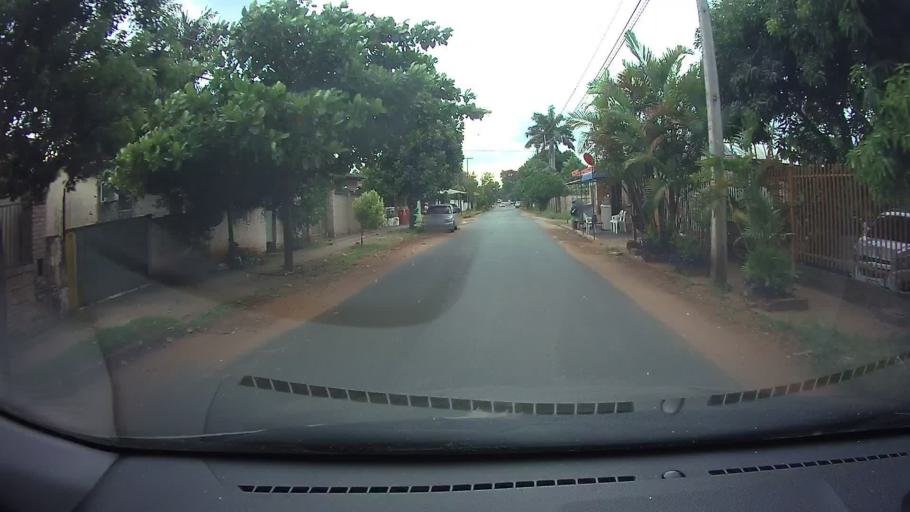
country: PY
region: Central
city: San Lorenzo
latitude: -25.2717
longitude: -57.4680
